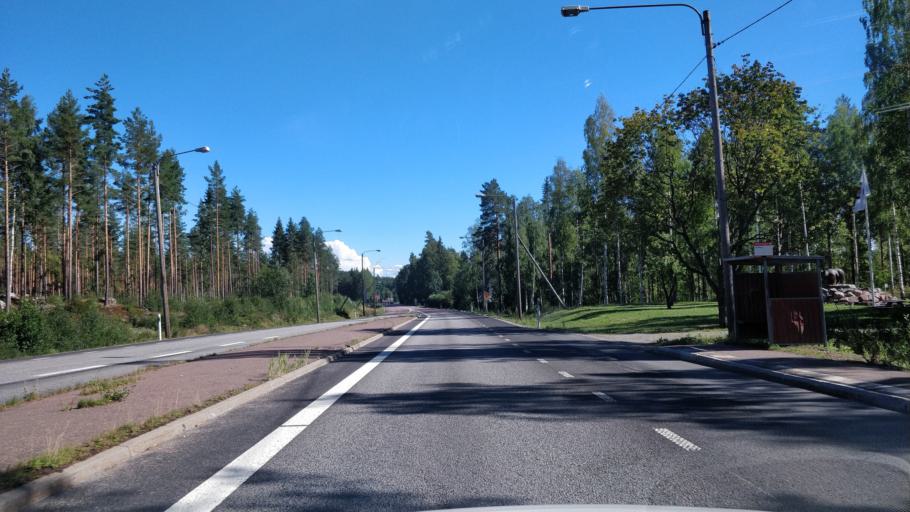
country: SE
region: Dalarna
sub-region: Faluns Kommun
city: Grycksbo
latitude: 60.6869
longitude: 15.4960
